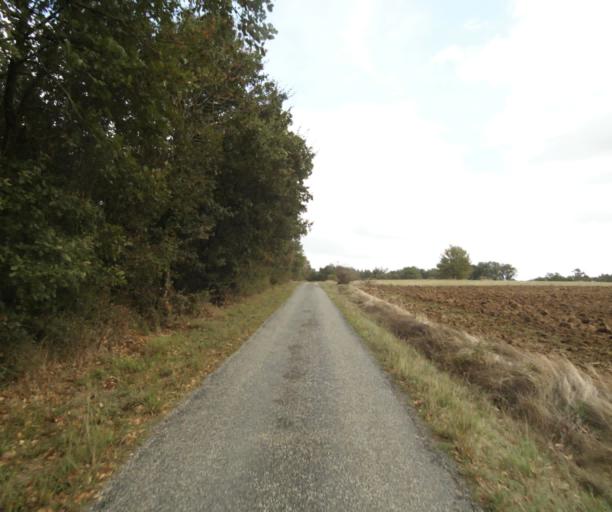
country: FR
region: Midi-Pyrenees
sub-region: Departement du Tarn-et-Garonne
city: Beaumont-de-Lomagne
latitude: 43.8675
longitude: 1.0937
